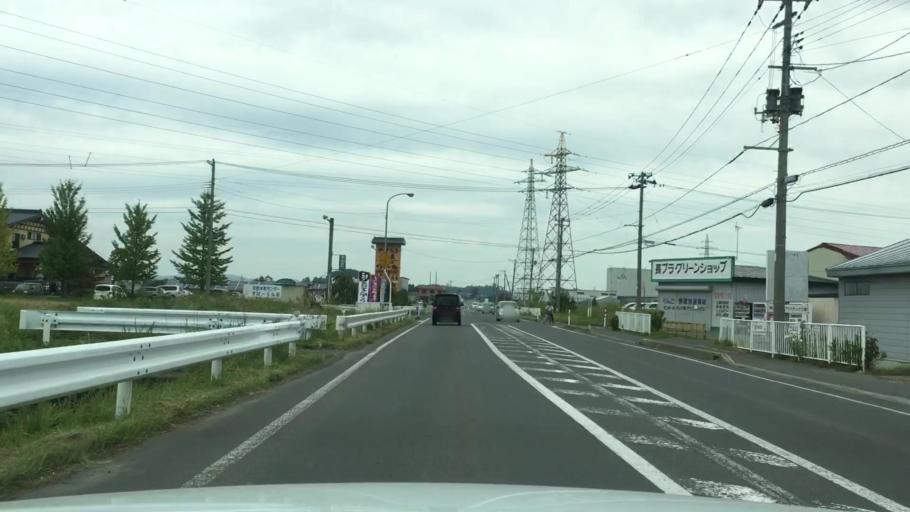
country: JP
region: Aomori
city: Hirosaki
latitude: 40.6327
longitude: 140.4511
